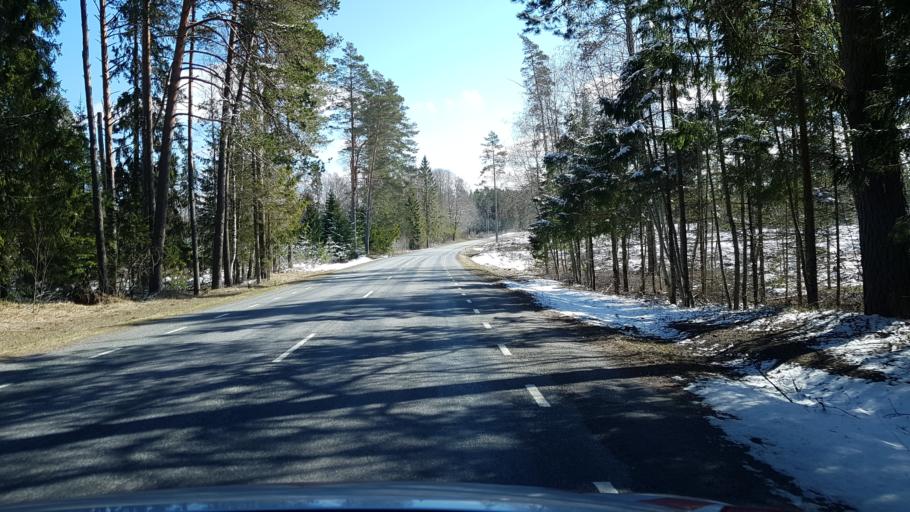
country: EE
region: Laeaene-Virumaa
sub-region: Tapa vald
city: Tapa
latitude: 59.4270
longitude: 25.9813
